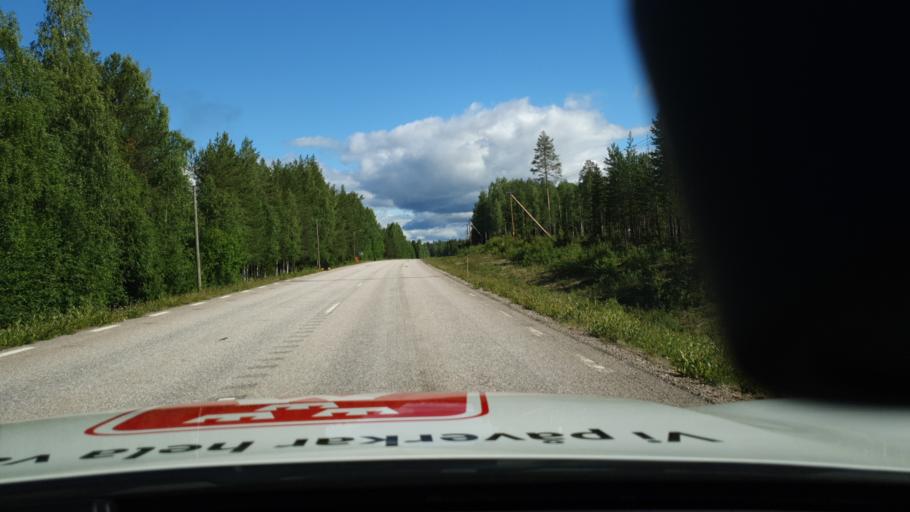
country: SE
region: Norrbotten
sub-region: Alvsbyns Kommun
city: AElvsbyn
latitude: 66.1851
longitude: 20.8794
